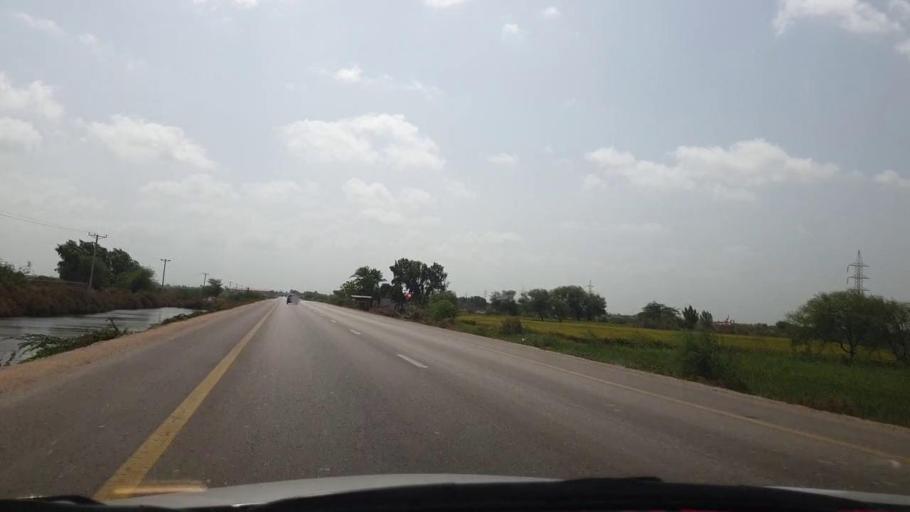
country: PK
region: Sindh
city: Talhar
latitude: 24.9207
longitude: 68.7230
